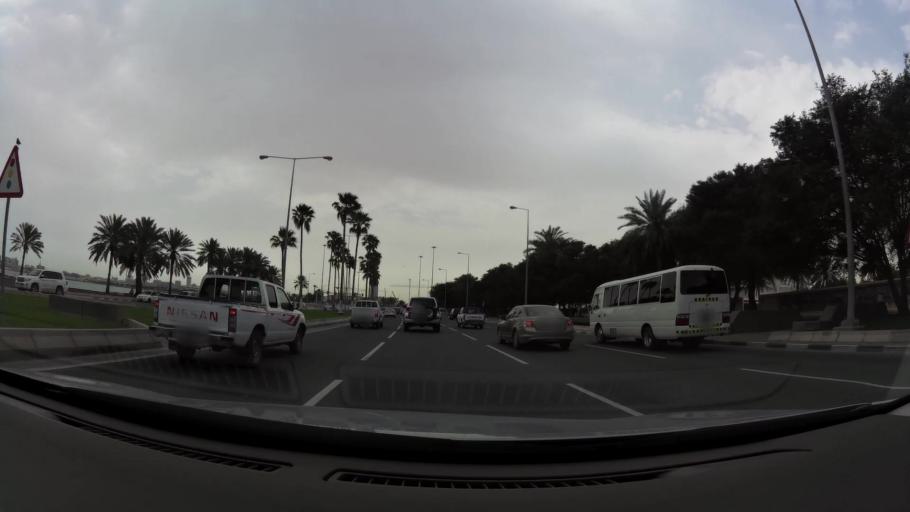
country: QA
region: Baladiyat ad Dawhah
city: Doha
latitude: 25.3061
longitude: 51.5178
